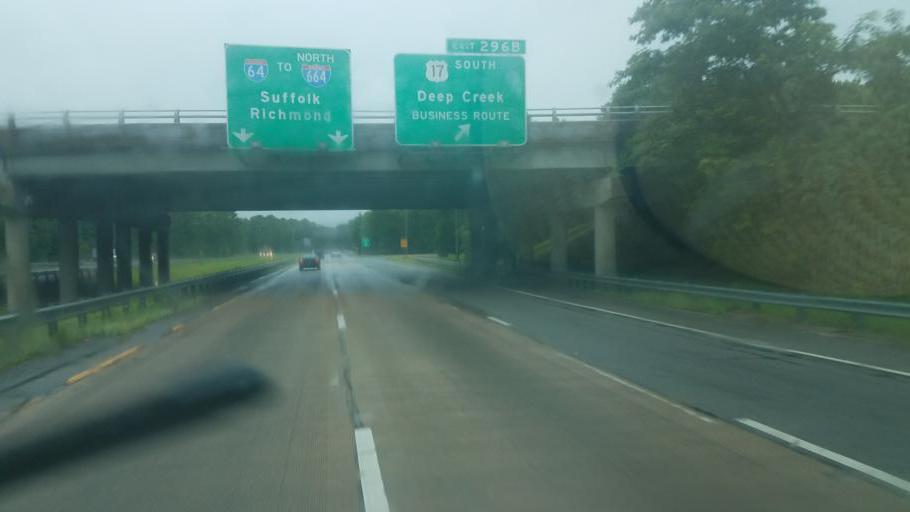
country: US
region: Virginia
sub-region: City of Portsmouth
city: Portsmouth Heights
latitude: 36.7588
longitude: -76.3442
